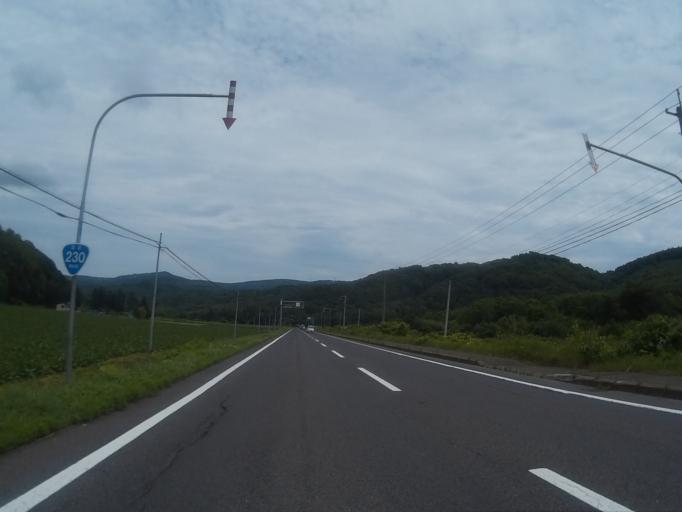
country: JP
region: Hokkaido
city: Niseko Town
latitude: 42.8000
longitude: 140.9813
